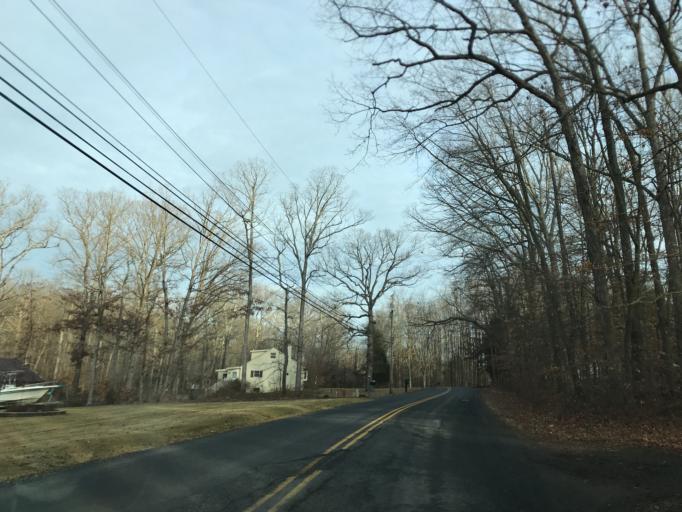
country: US
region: Maryland
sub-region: Harford County
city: Joppatowne
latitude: 39.4511
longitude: -76.3685
